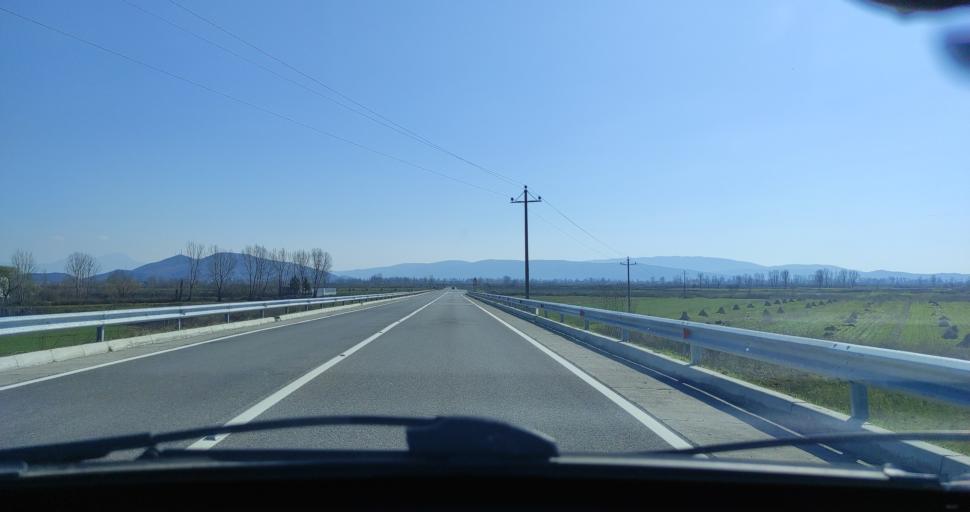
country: AL
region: Shkoder
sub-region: Rrethi i Shkodres
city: Berdica e Madhe
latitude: 42.0083
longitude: 19.4782
